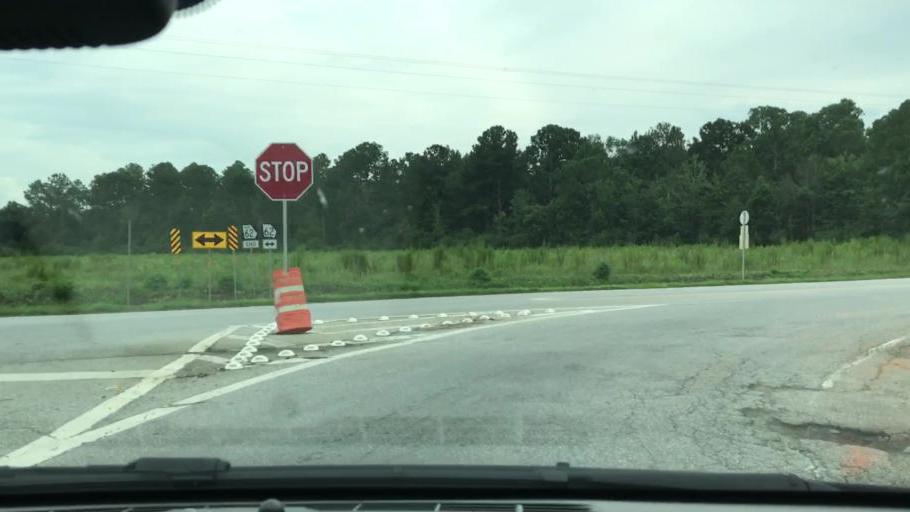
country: US
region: Georgia
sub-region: Early County
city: Blakely
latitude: 31.3690
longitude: -84.9575
